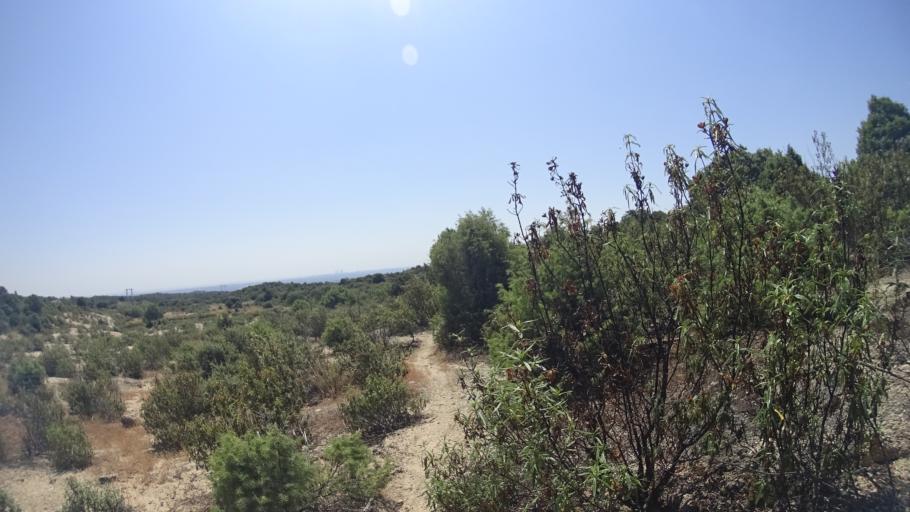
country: ES
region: Madrid
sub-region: Provincia de Madrid
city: Torrelodones
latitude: 40.5969
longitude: -3.9221
